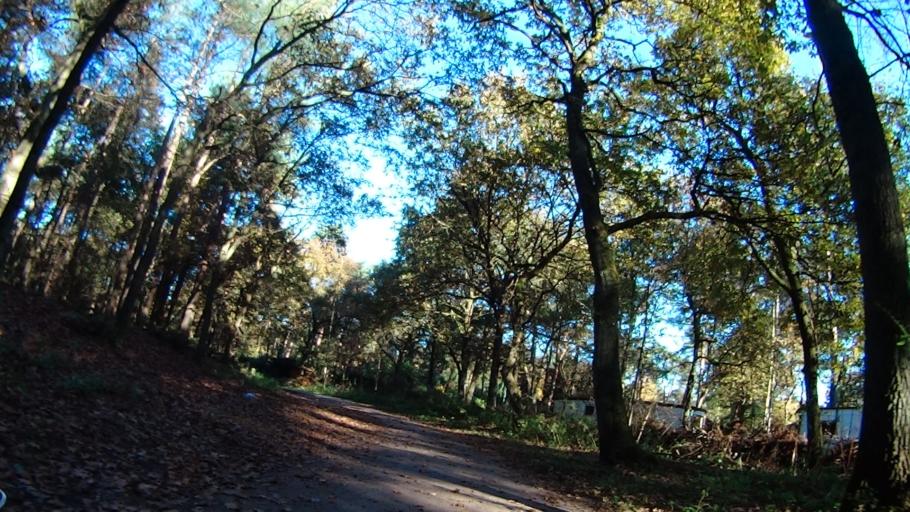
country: NL
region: Utrecht
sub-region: Gemeente Soest
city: Soest
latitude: 52.1513
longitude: 5.3287
